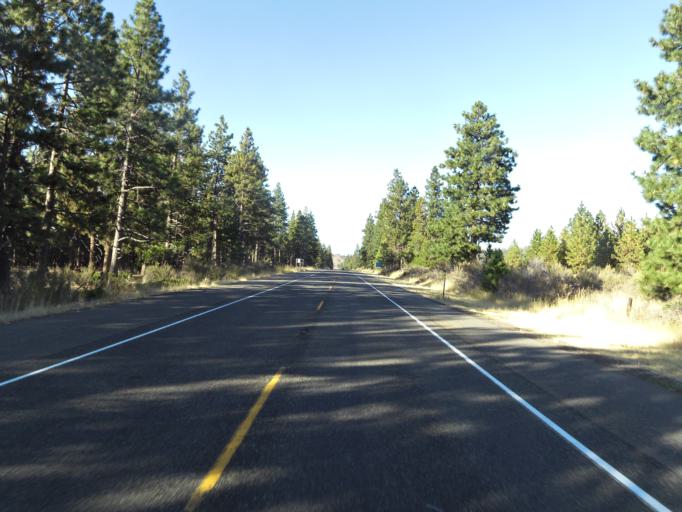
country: US
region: California
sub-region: Siskiyou County
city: Weed
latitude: 41.4582
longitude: -122.3571
